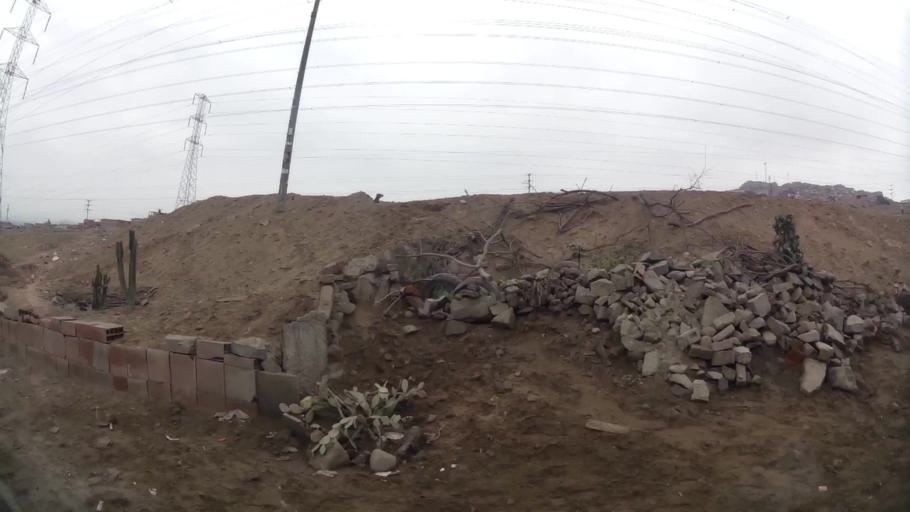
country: PE
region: Lima
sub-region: Lima
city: Surco
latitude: -12.1819
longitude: -76.9595
